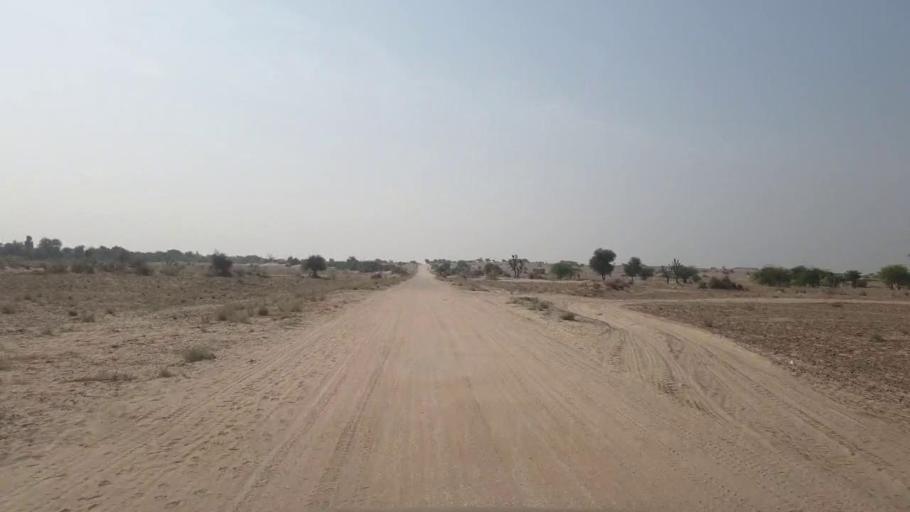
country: PK
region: Sindh
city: Umarkot
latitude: 25.3064
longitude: 69.7285
